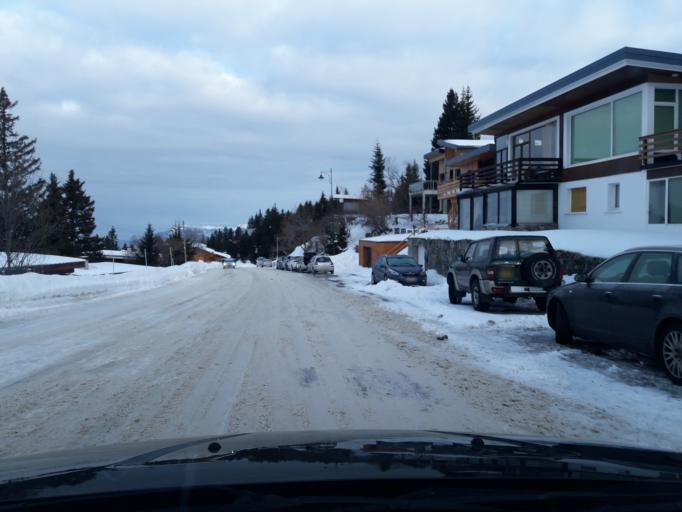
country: FR
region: Rhone-Alpes
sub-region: Departement de l'Isere
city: Vaulnaveys-le-Bas
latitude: 45.1135
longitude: 5.8774
